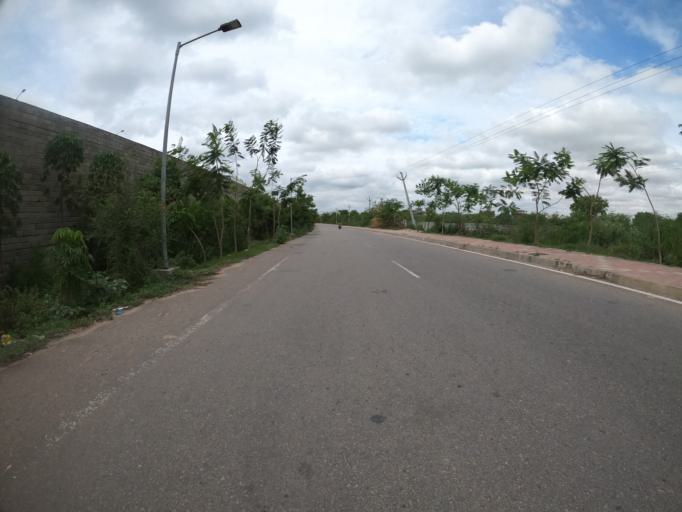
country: IN
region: Telangana
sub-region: Rangareddi
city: Sriramnagar
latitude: 17.2604
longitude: 78.3754
